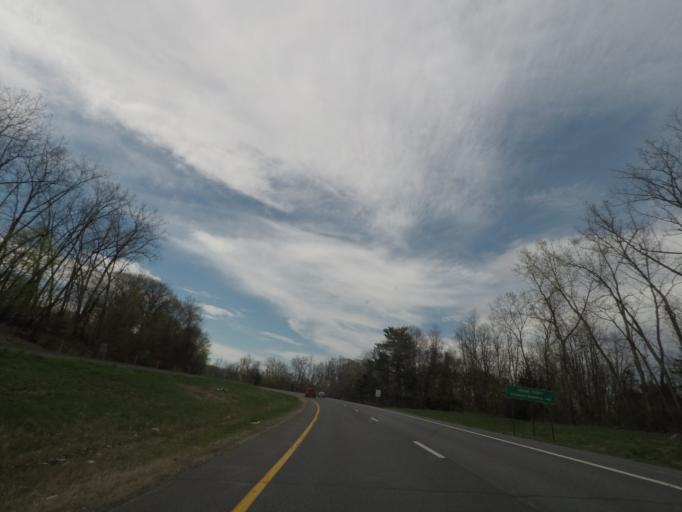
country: US
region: New York
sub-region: Greene County
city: Jefferson Heights
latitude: 42.2353
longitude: -73.8728
